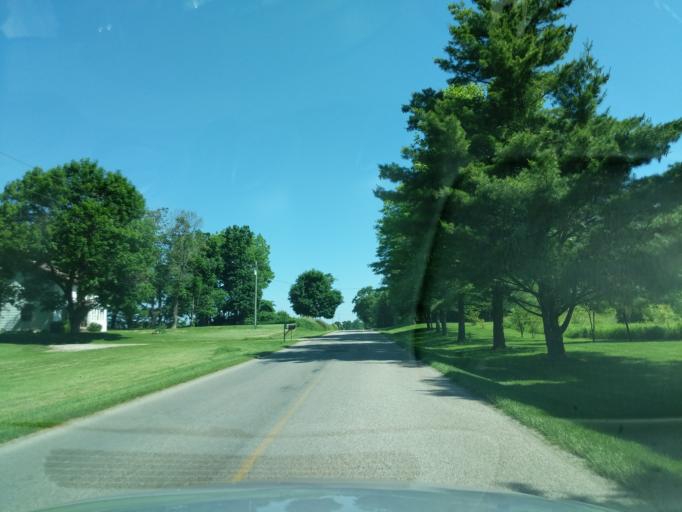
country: US
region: Indiana
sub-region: Huntington County
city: Huntington
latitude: 40.8408
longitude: -85.5088
